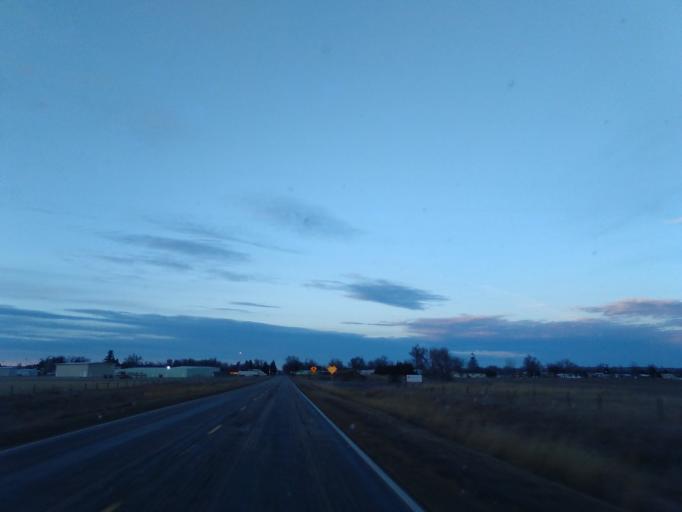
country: US
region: Nebraska
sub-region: Garden County
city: Oshkosh
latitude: 41.3972
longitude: -102.3476
